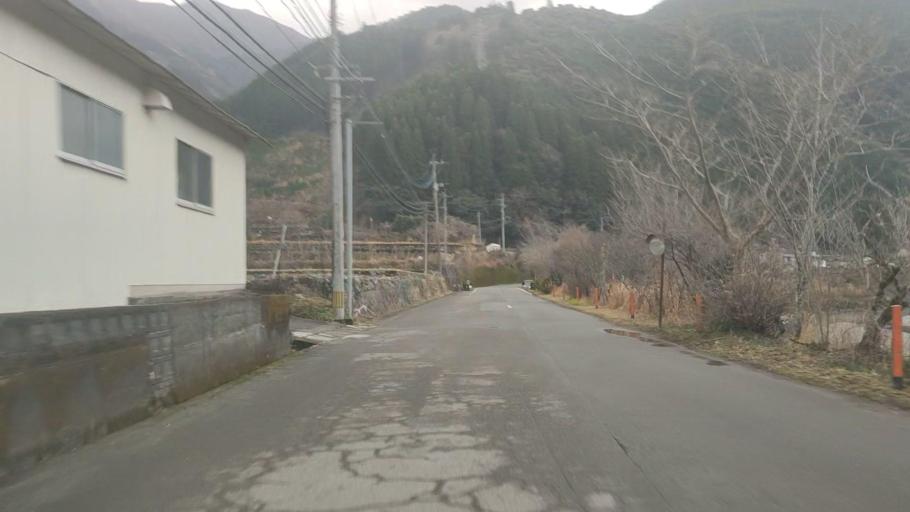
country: JP
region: Kumamoto
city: Hitoyoshi
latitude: 32.4355
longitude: 130.8589
